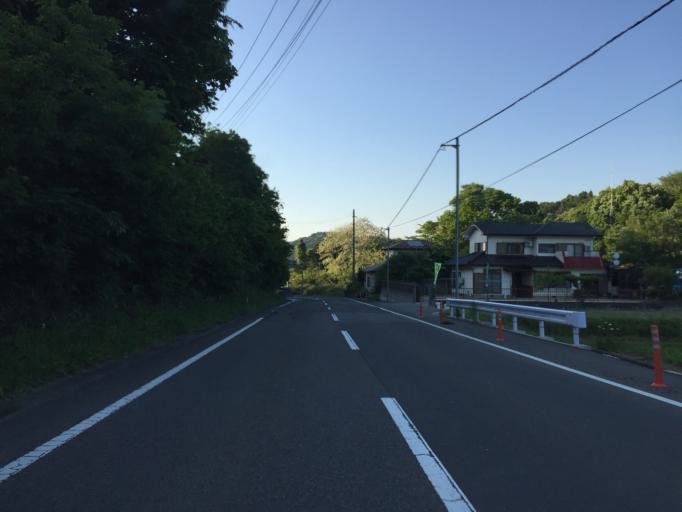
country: JP
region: Fukushima
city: Ishikawa
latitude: 37.0712
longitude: 140.4240
